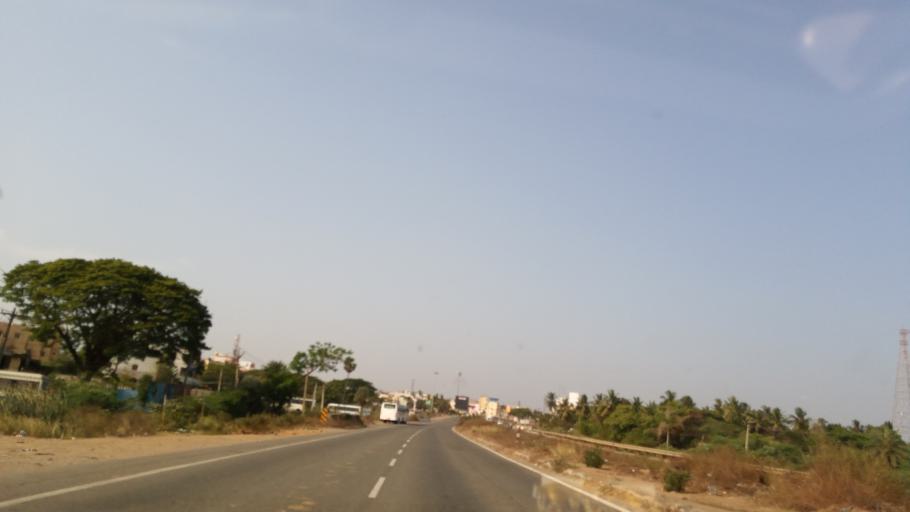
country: IN
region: Tamil Nadu
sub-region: Kancheepuram
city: Sriperumbudur
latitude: 12.9722
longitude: 79.9556
